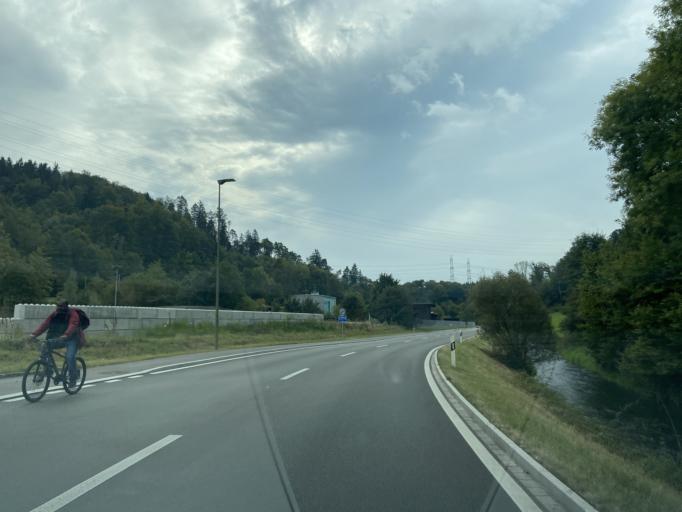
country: CH
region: Zurich
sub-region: Bezirk Pfaeffikon
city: Effretikon / Watt
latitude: 47.4405
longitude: 8.7036
